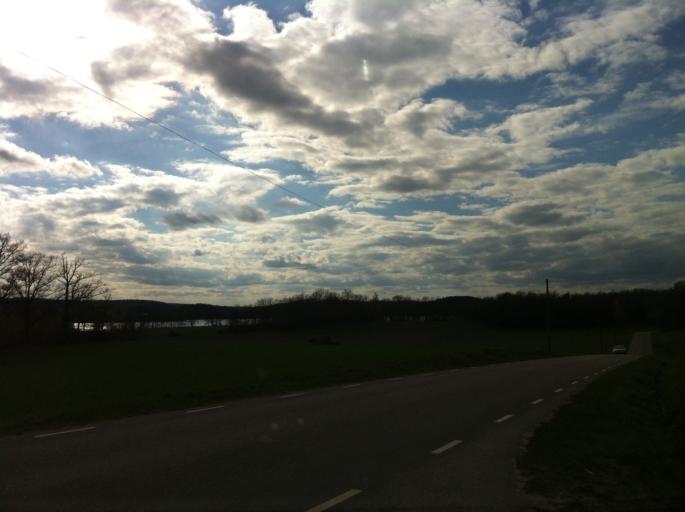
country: SE
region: OEstergoetland
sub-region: Kinda Kommun
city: Rimforsa
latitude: 58.0393
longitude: 15.8094
